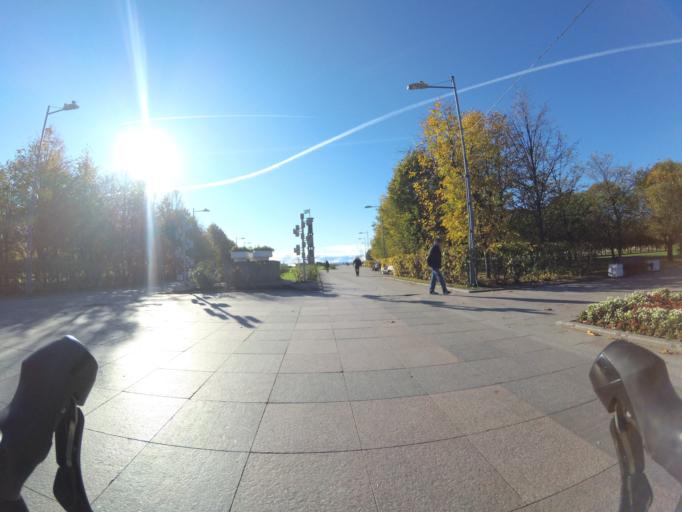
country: RU
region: Leningrad
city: Untolovo
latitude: 59.9830
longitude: 30.2014
